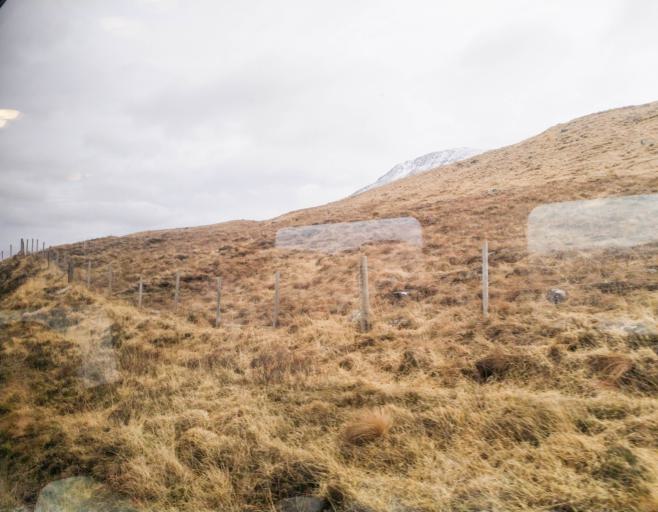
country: GB
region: Scotland
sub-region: Highland
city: Spean Bridge
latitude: 56.5513
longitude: -4.7471
